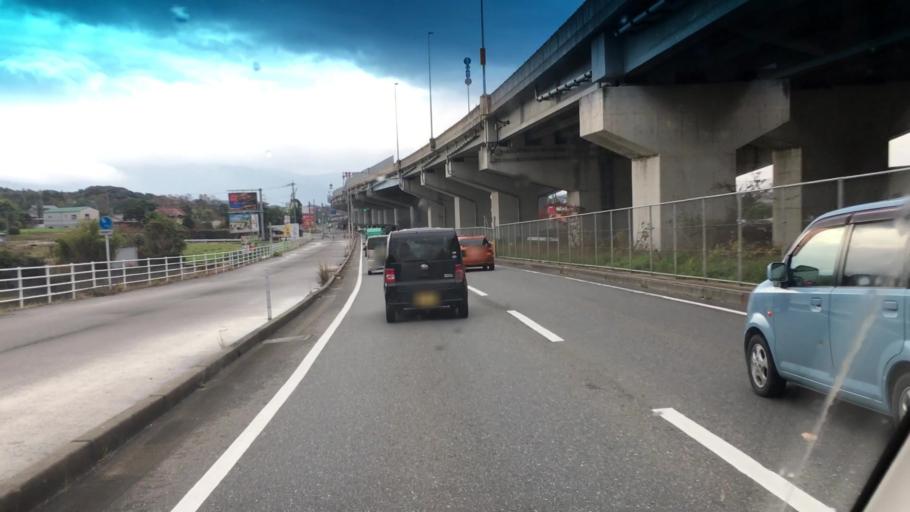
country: JP
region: Fukuoka
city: Maebaru-chuo
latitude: 33.5708
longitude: 130.2508
